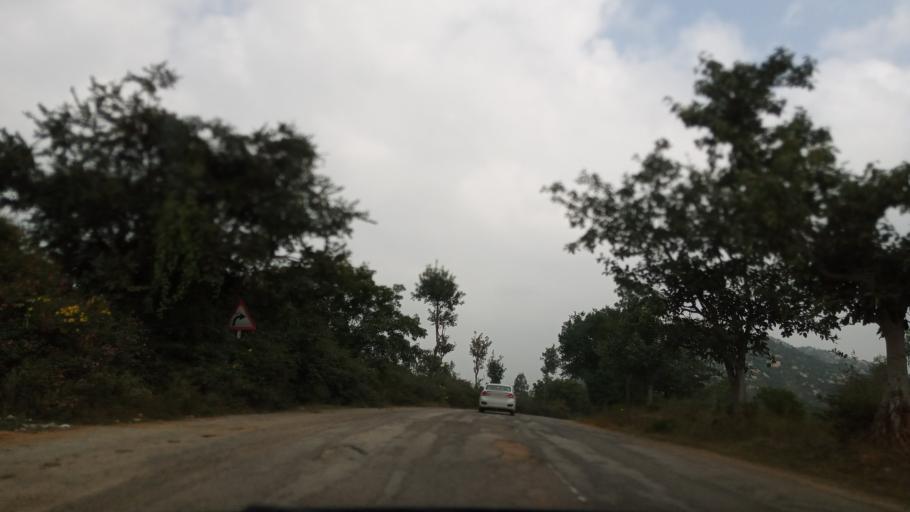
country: IN
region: Andhra Pradesh
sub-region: Chittoor
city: Madanapalle
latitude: 13.5112
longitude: 78.3368
